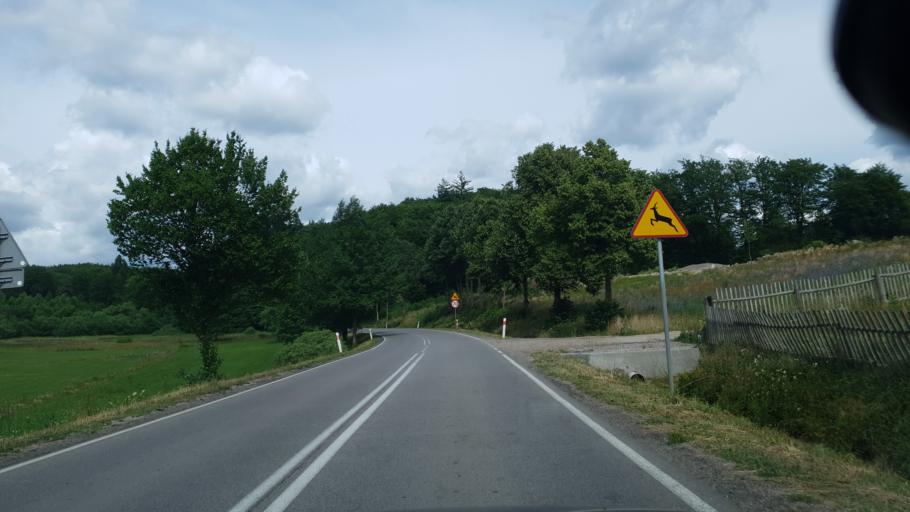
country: PL
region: Pomeranian Voivodeship
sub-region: Powiat kartuski
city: Kartuzy
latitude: 54.3134
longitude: 18.1604
